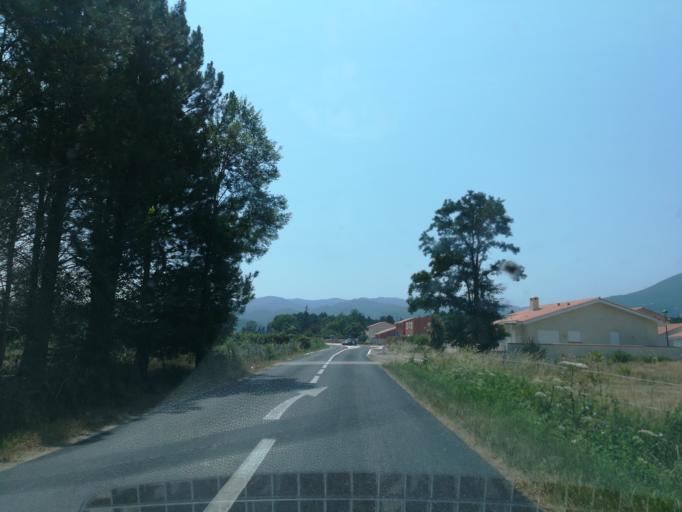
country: FR
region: Languedoc-Roussillon
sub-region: Departement des Pyrenees-Orientales
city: Sant Joan de Pladecorts
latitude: 42.5001
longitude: 2.7983
